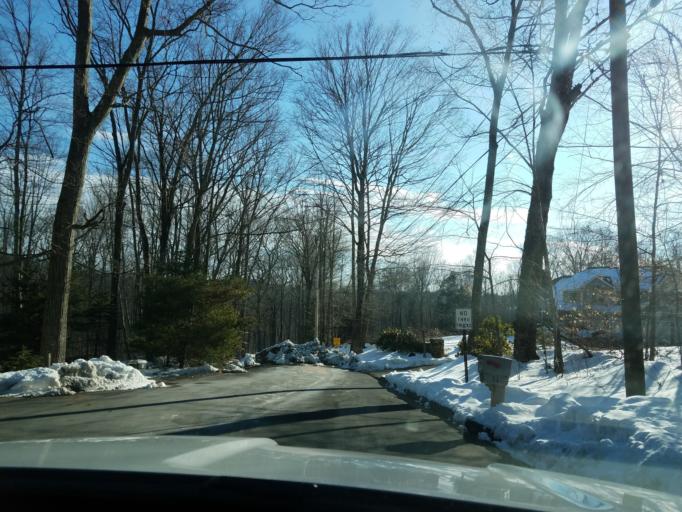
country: US
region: Connecticut
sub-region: Litchfield County
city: Bethlehem Village
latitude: 41.6293
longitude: -73.2330
